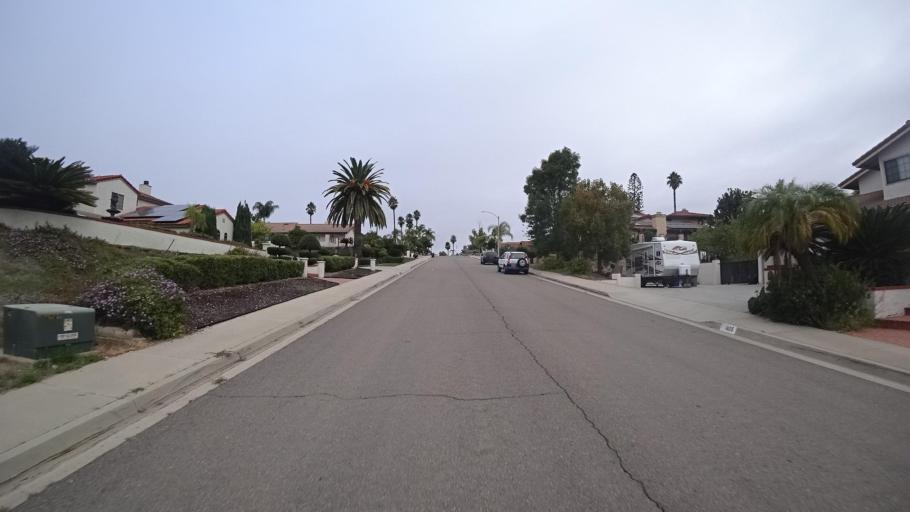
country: US
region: California
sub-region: San Diego County
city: Rancho San Diego
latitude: 32.7585
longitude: -116.9143
